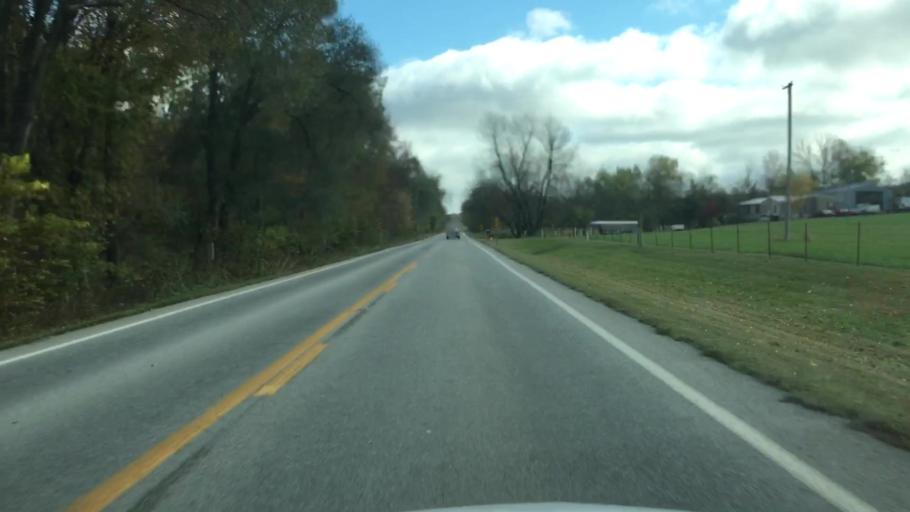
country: US
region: Arkansas
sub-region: Benton County
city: Gentry
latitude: 36.2604
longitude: -94.4160
